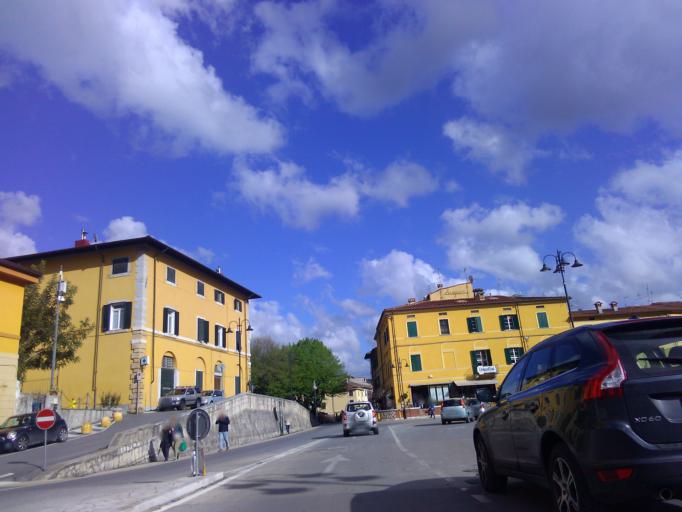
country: IT
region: Tuscany
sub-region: Provincia di Lucca
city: Pietrasanta
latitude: 43.9600
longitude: 10.2280
